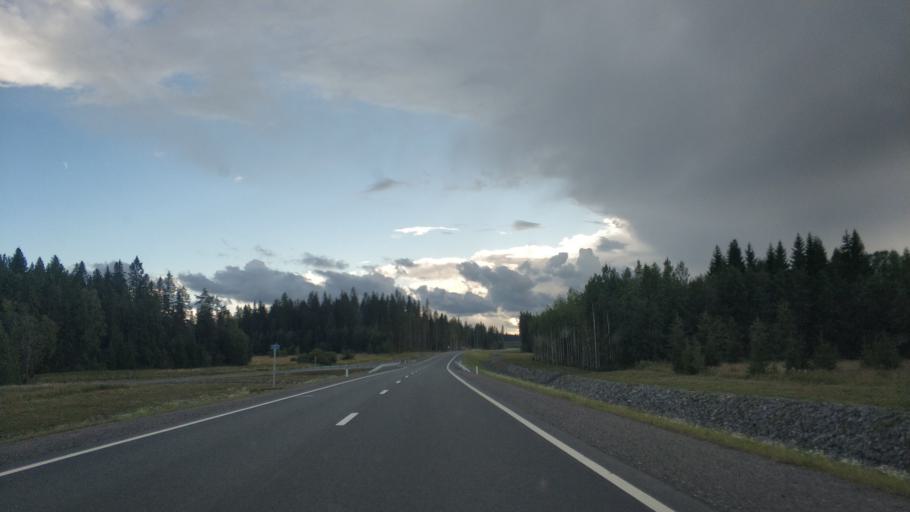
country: RU
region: Republic of Karelia
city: Lakhdenpokh'ya
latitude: 61.4542
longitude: 29.9975
